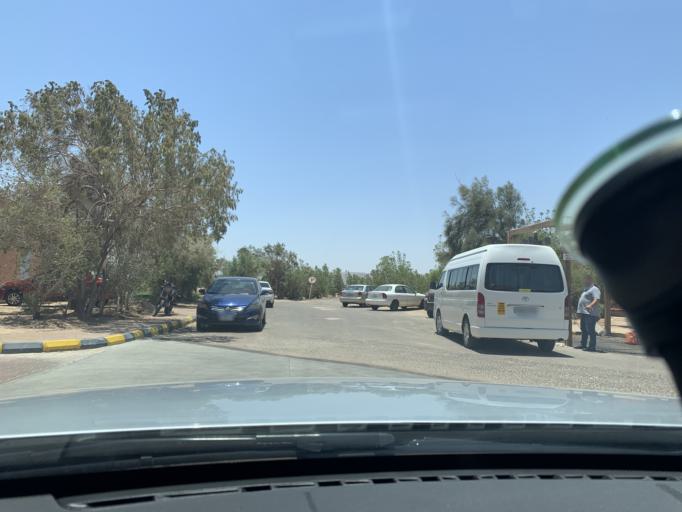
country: EG
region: Red Sea
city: El Gouna
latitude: 27.3955
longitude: 33.6696
